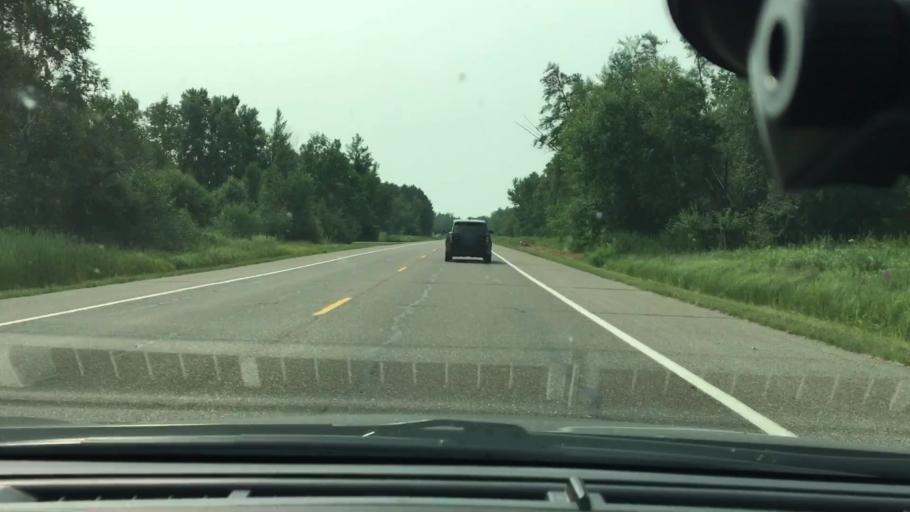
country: US
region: Minnesota
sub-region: Crow Wing County
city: Brainerd
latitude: 46.3924
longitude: -94.2233
